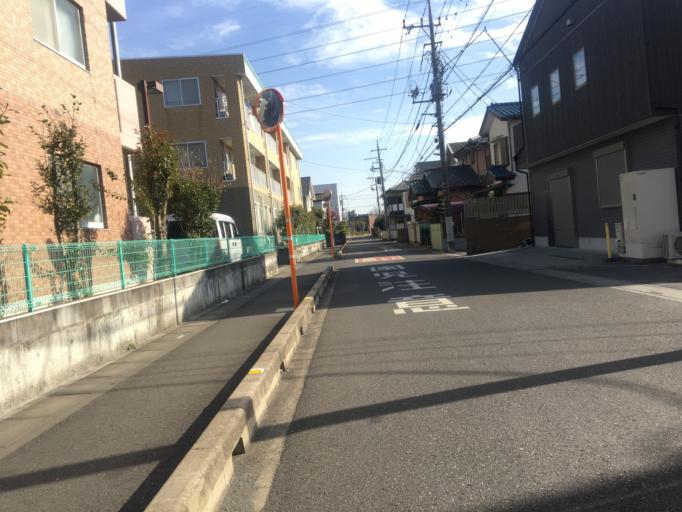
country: JP
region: Saitama
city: Shiki
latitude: 35.8426
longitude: 139.5865
